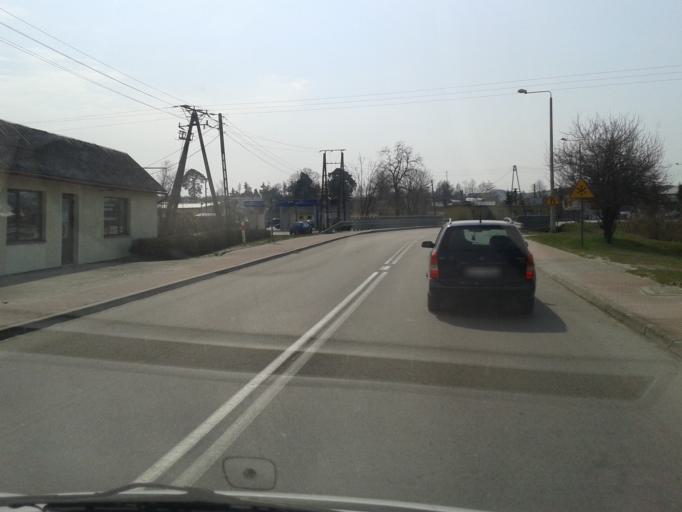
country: PL
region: Subcarpathian Voivodeship
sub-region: Powiat lubaczowski
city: Narol
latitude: 50.3474
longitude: 23.3269
